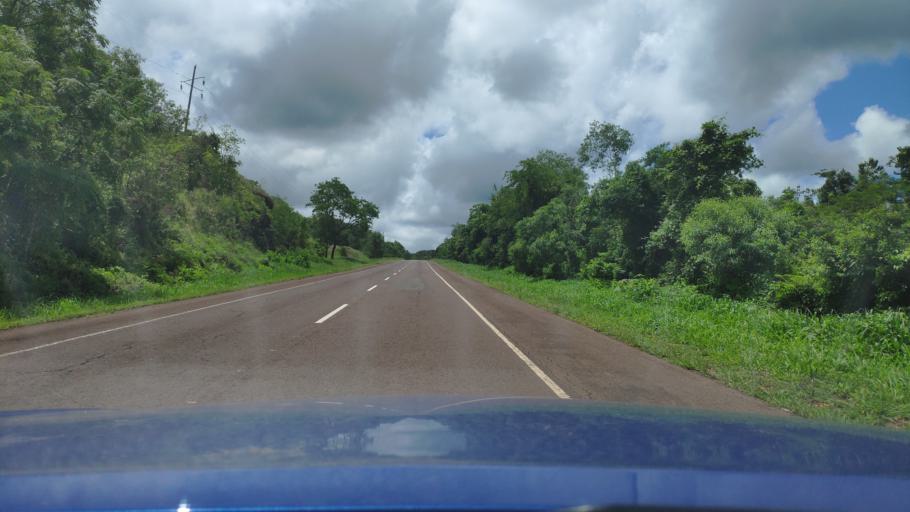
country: AR
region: Misiones
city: Dos Arroyos
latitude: -27.7586
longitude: -55.2479
